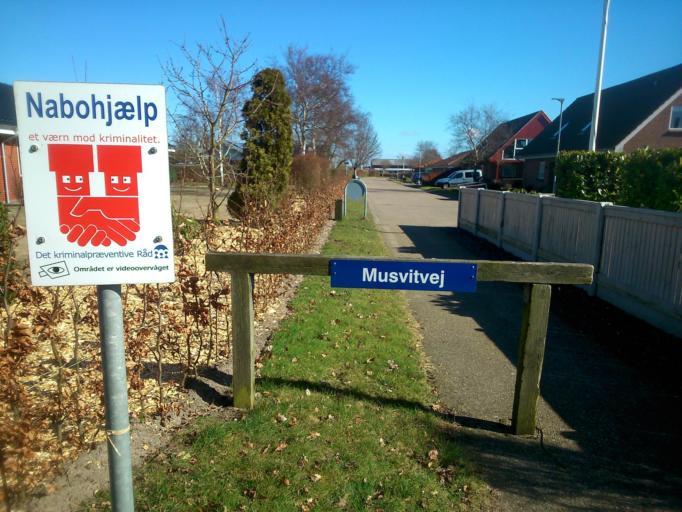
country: DK
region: Central Jutland
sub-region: Ringkobing-Skjern Kommune
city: Ringkobing
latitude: 56.0884
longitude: 8.2631
